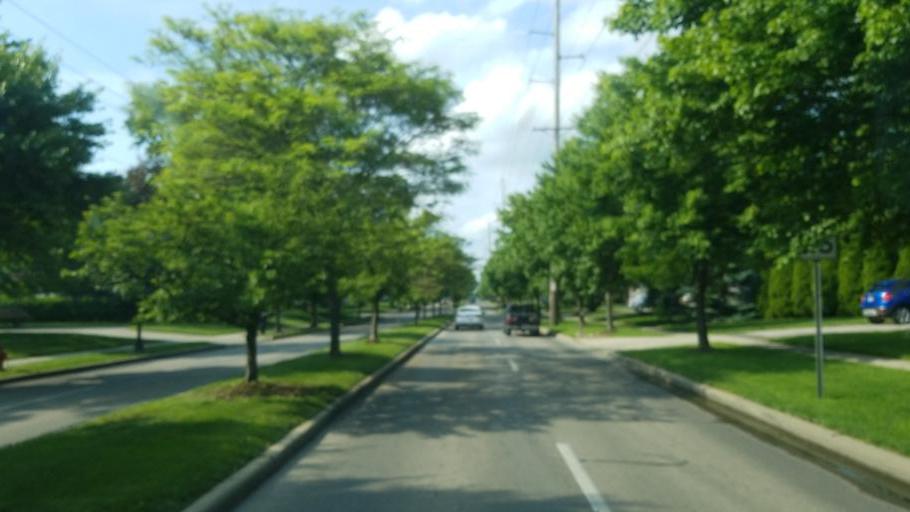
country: US
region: Ohio
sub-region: Franklin County
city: Westerville
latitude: 40.1260
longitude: -82.9033
